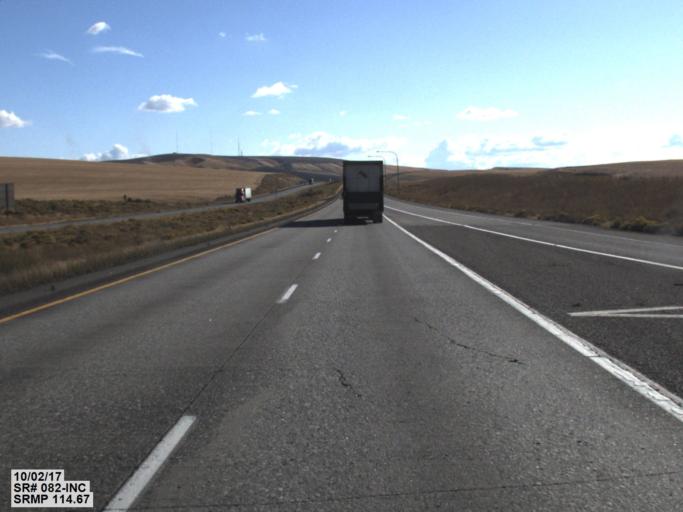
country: US
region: Washington
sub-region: Benton County
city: Highland
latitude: 46.1385
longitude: -119.2023
